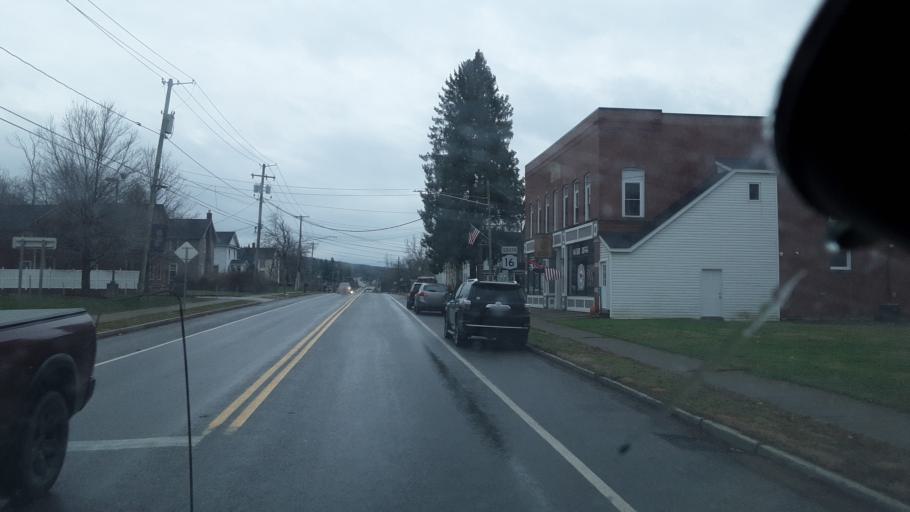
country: US
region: New York
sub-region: Erie County
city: Holland
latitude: 42.6411
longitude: -78.5419
